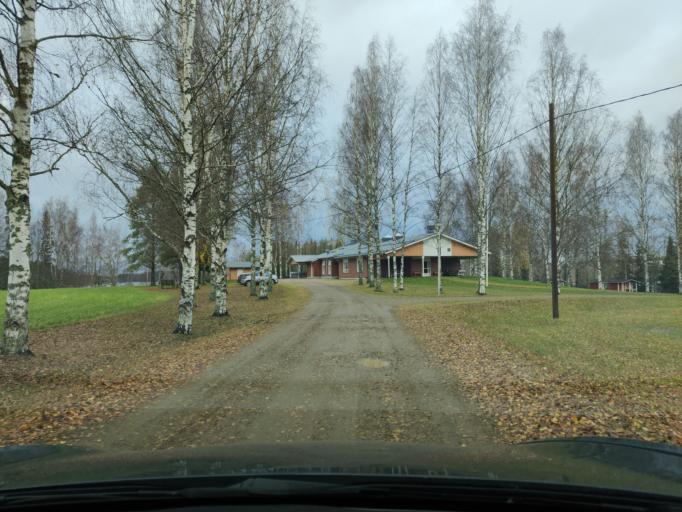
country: FI
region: Northern Savo
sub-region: Ylae-Savo
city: Kiuruvesi
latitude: 63.6412
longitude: 26.6545
